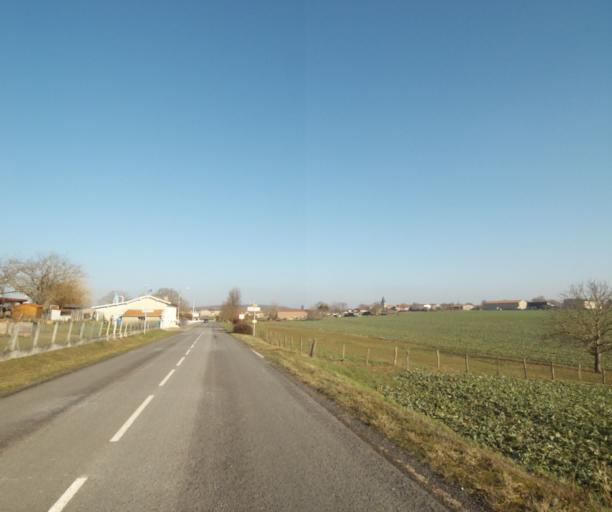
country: FR
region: Champagne-Ardenne
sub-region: Departement de la Haute-Marne
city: Wassy
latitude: 48.5111
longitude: 4.9983
